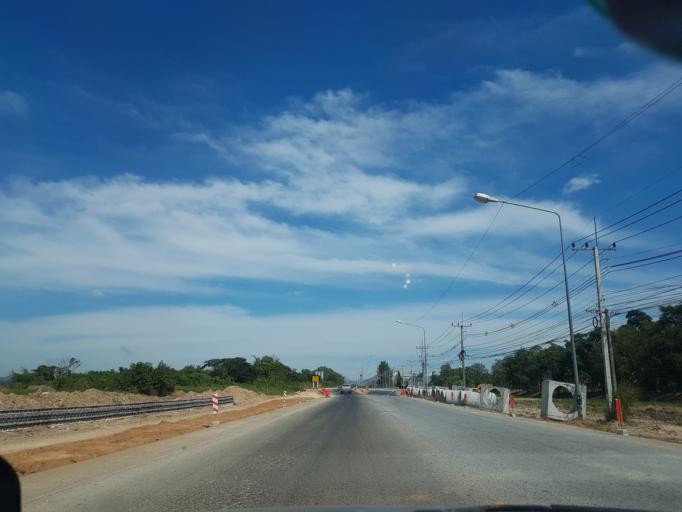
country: TH
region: Chon Buri
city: Sattahip
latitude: 12.6613
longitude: 100.9677
